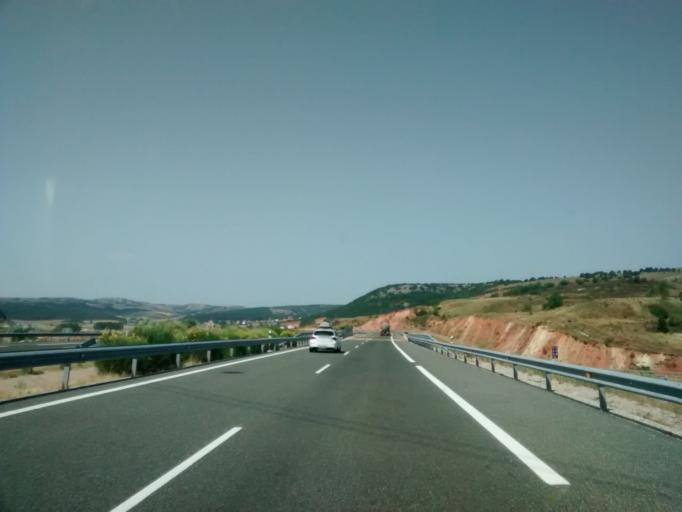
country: ES
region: Castille and Leon
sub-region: Provincia de Palencia
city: Aguilar de Campoo
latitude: 42.7705
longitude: -4.2700
